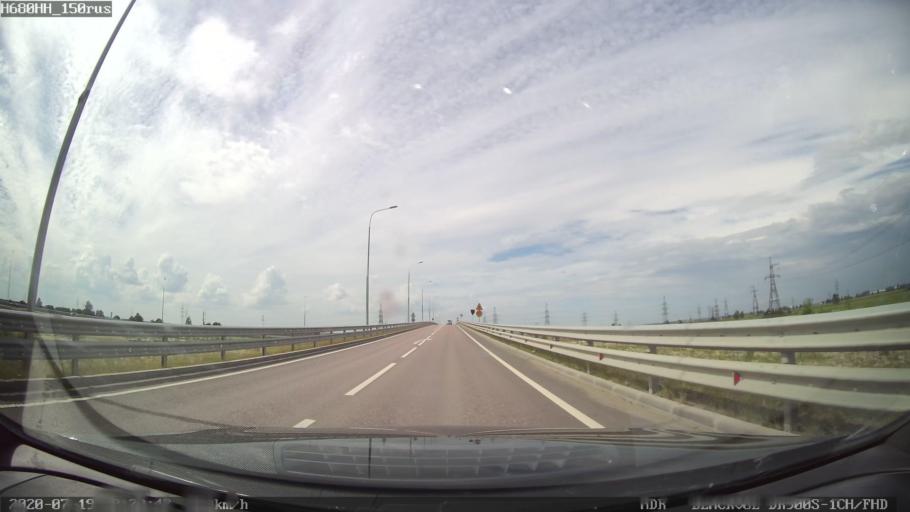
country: RU
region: Leningrad
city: Fedorovskoye
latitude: 59.7071
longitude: 30.5478
